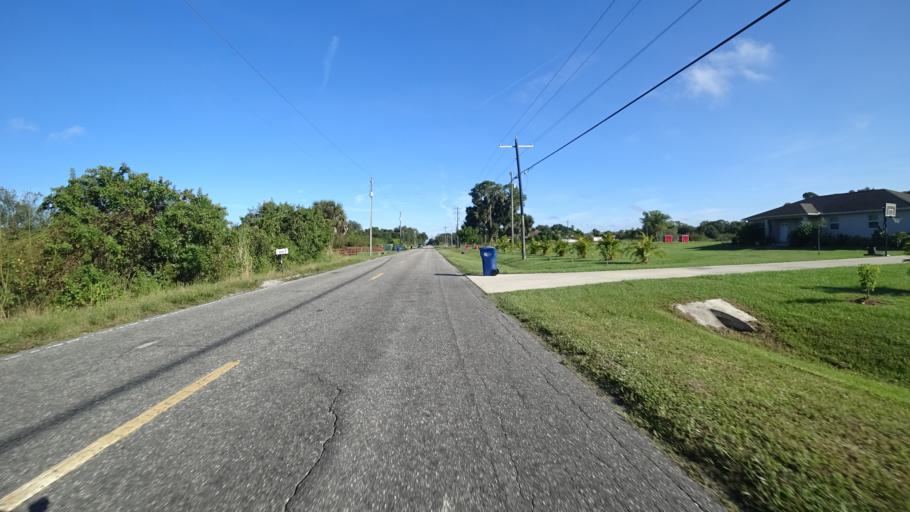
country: US
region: Florida
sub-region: Manatee County
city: Memphis
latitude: 27.5958
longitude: -82.5274
